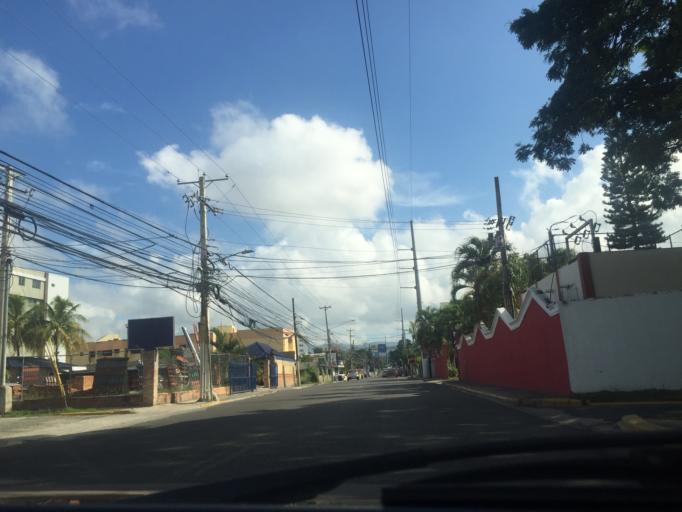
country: DO
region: Santiago
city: Santiago de los Caballeros
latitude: 19.4498
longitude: -70.6657
